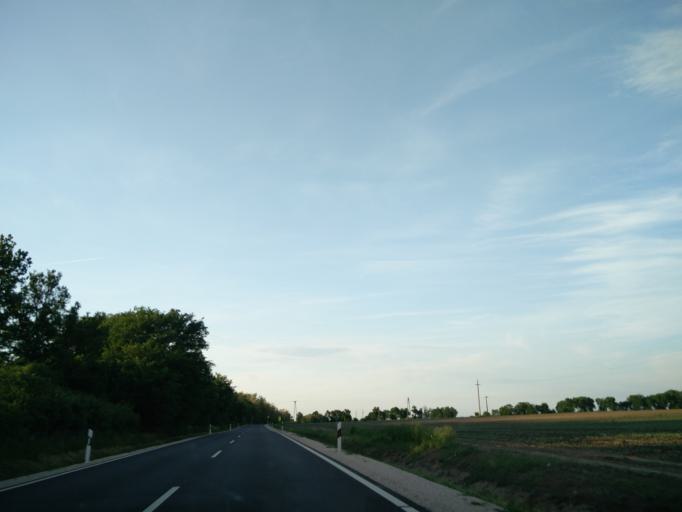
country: HU
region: Fejer
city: Lovasbereny
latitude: 47.2816
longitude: 18.5270
